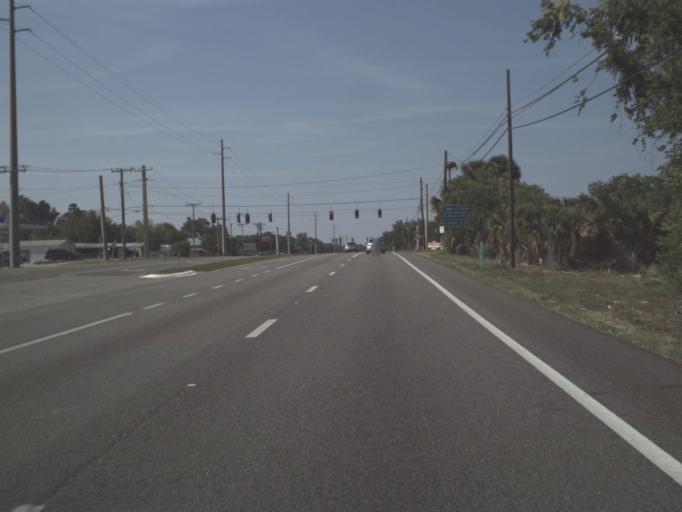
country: US
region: Florida
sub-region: Brevard County
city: Sharpes
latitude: 28.4455
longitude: -80.7630
